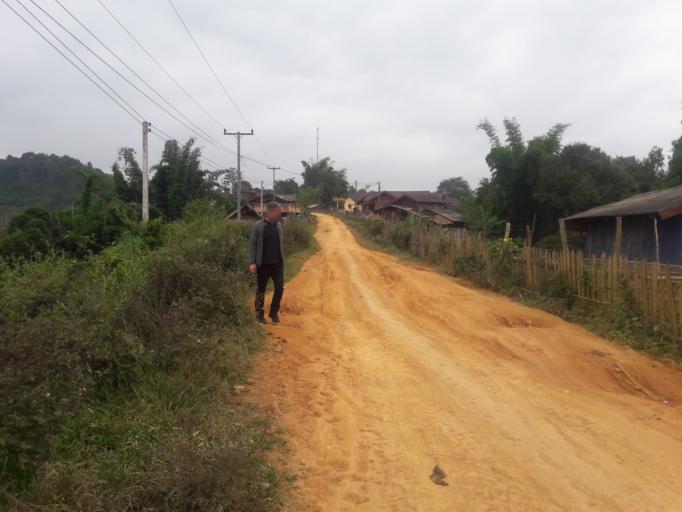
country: LA
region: Xiangkhoang
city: Muang Phonsavan
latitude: 19.3363
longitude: 103.4979
